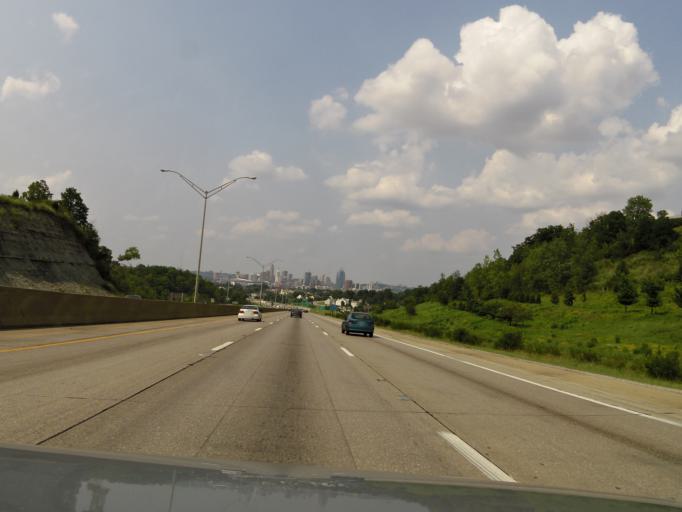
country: US
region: Kentucky
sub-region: Kenton County
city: Park Hills
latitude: 39.0670
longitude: -84.5206
